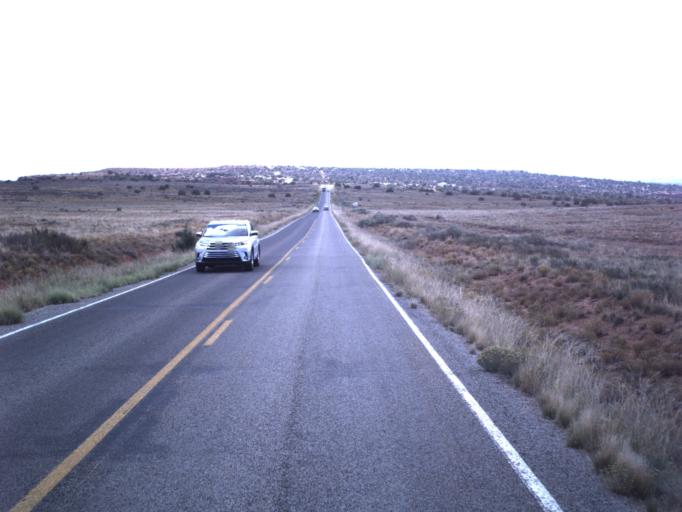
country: US
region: Utah
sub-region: Grand County
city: Moab
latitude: 38.5019
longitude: -109.7317
